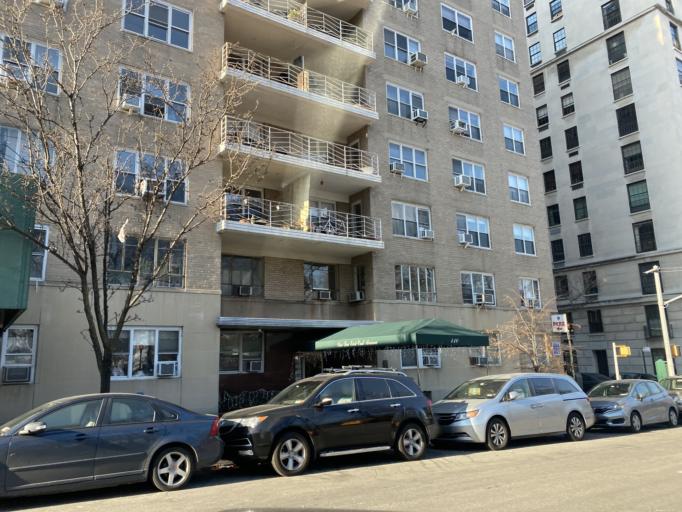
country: US
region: New York
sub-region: New York County
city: Manhattan
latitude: 40.7740
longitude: -73.9454
